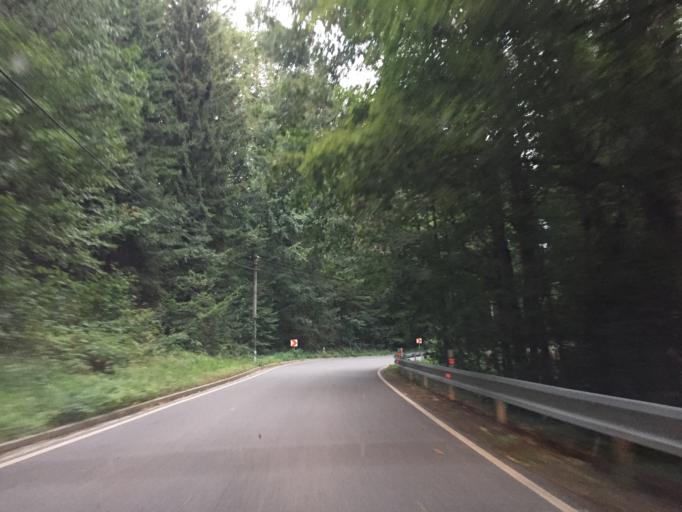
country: CZ
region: Liberecky
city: Mala Skala
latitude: 50.6544
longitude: 15.1990
